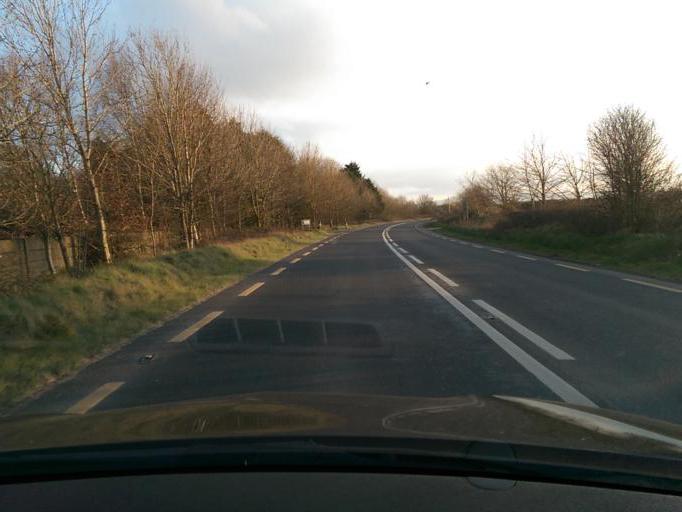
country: IE
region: Munster
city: Nenagh Bridge
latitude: 52.8934
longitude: -8.1881
